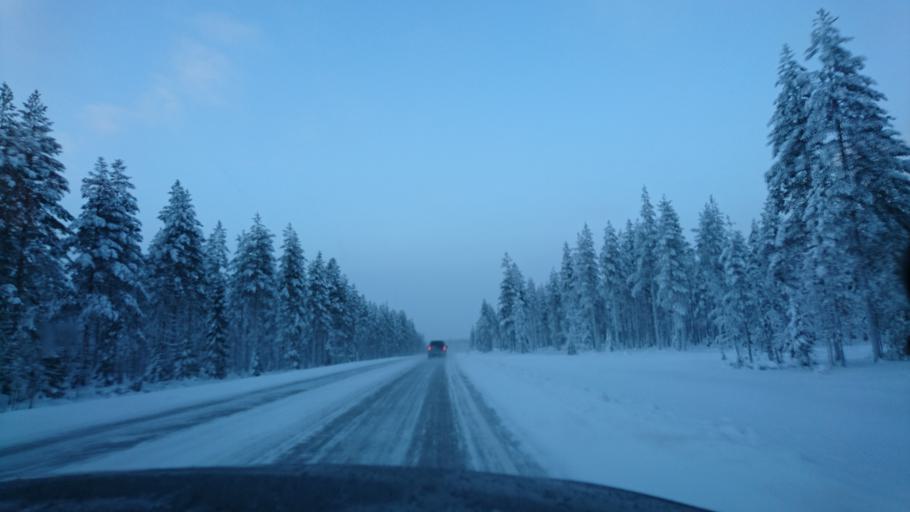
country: FI
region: Northern Ostrobothnia
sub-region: Koillismaa
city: Taivalkoski
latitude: 65.4762
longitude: 27.7751
